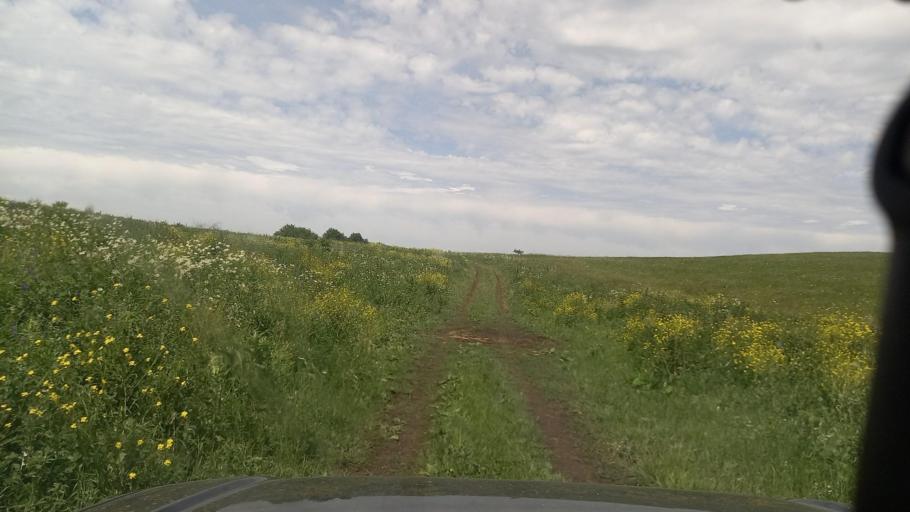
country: RU
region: Krasnodarskiy
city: Peredovaya
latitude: 44.0709
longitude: 41.3182
